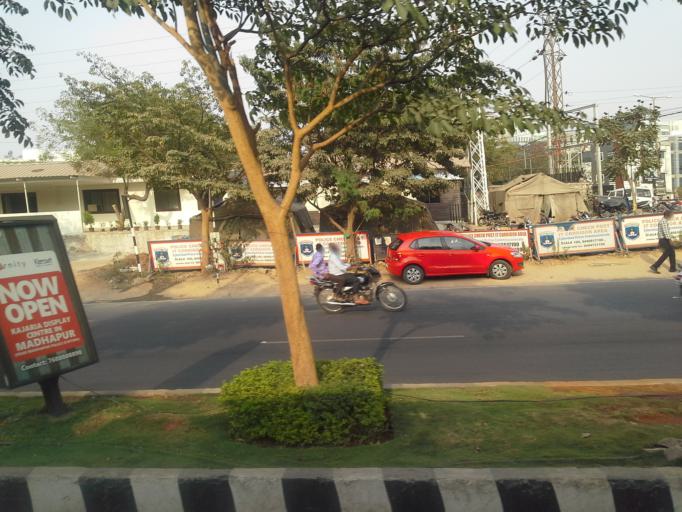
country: IN
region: Telangana
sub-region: Medak
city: Serilingampalle
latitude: 17.4456
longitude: 78.3519
